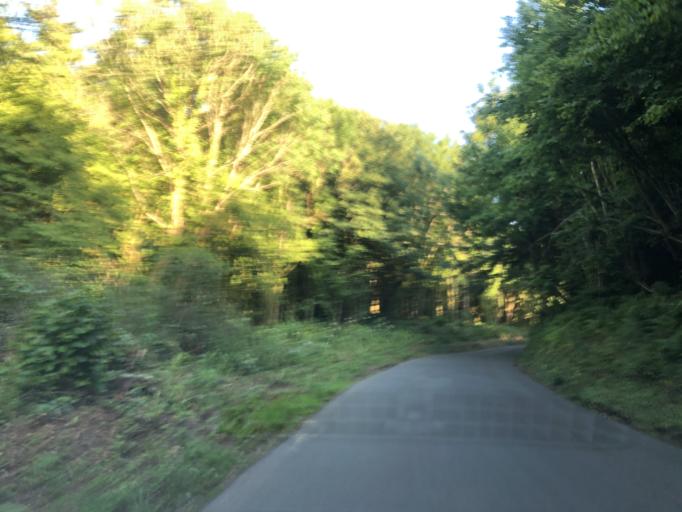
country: GB
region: England
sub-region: Isle of Wight
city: Shalfleet
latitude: 50.6611
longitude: -1.4068
